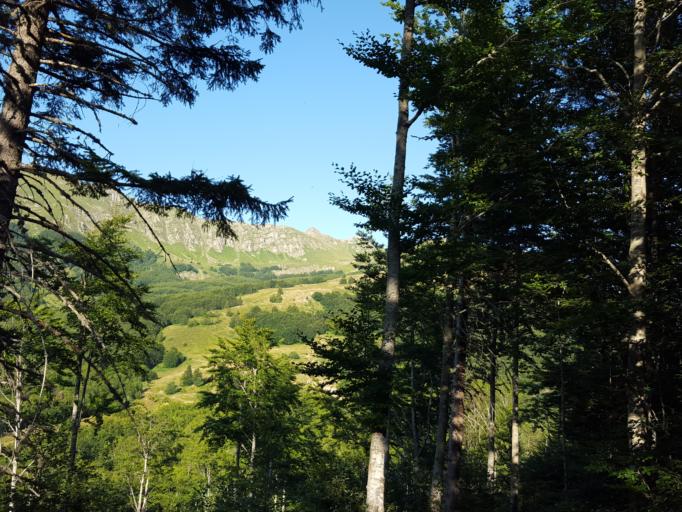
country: IT
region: Tuscany
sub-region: Provincia di Pistoia
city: Abetone
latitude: 44.1570
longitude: 10.6846
